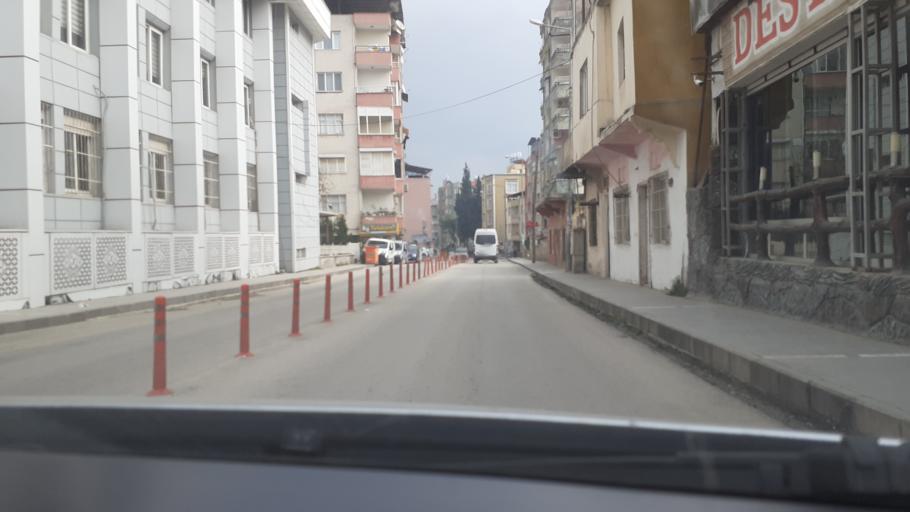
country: TR
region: Hatay
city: Kirikhan
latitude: 36.4985
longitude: 36.3518
